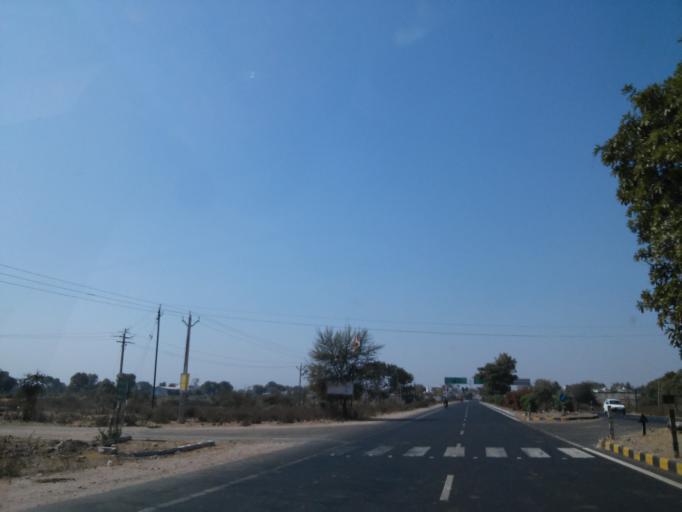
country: IN
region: Gujarat
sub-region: Sabar Kantha
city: Himatnagar
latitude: 23.5817
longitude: 73.0063
